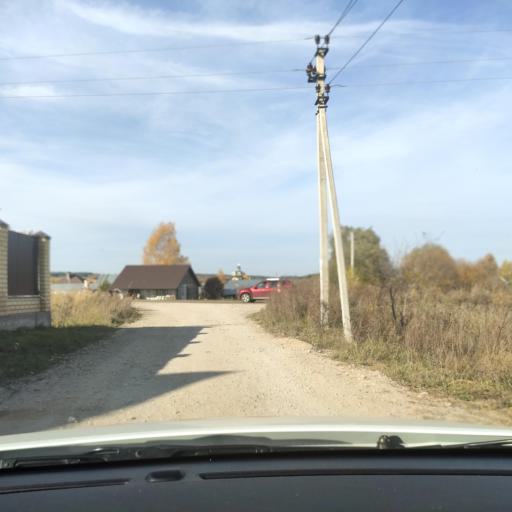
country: RU
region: Tatarstan
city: Vysokaya Gora
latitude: 55.7484
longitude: 49.4064
